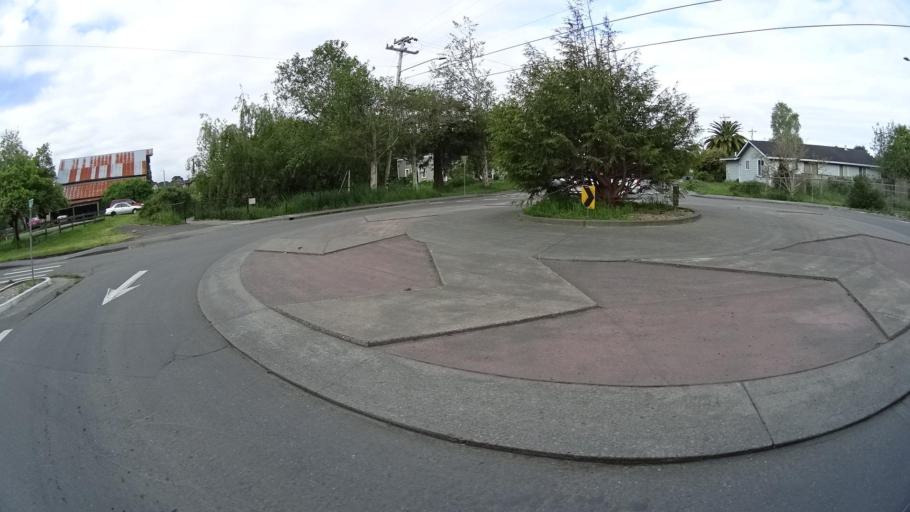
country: US
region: California
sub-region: Humboldt County
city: Arcata
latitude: 40.8893
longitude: -124.0820
